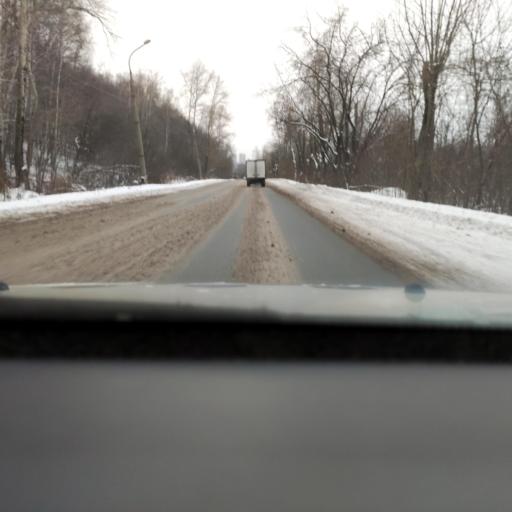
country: RU
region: Perm
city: Perm
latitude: 58.0824
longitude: 56.3509
